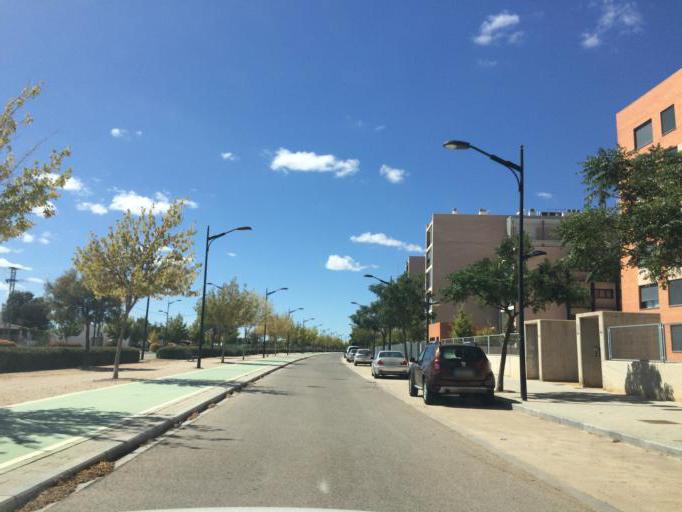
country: ES
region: Castille-La Mancha
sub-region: Provincia de Albacete
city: Albacete
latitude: 38.9791
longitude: -1.8362
